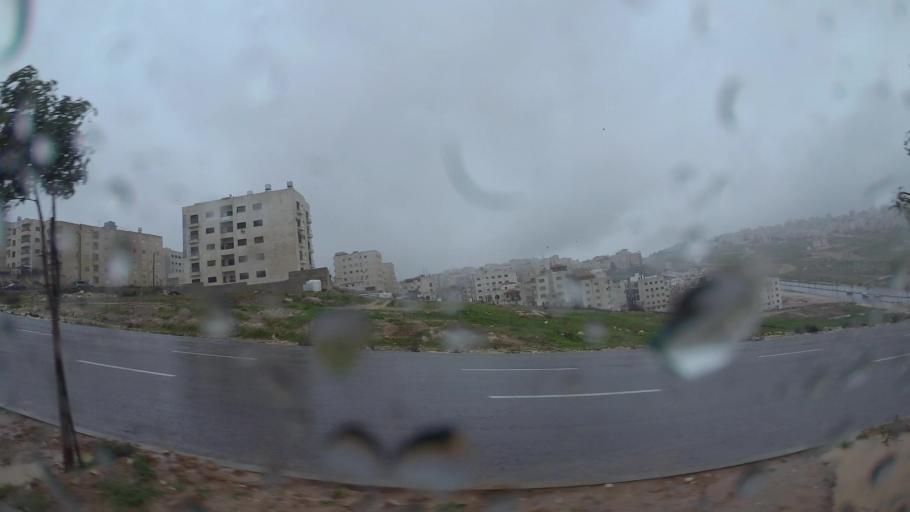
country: JO
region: Amman
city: Al Jubayhah
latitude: 32.0379
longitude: 35.8843
